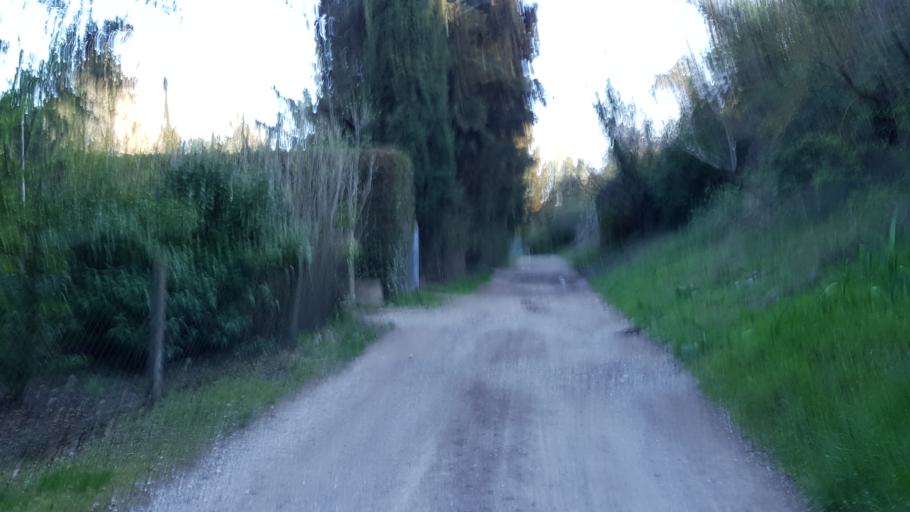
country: FR
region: Provence-Alpes-Cote d'Azur
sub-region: Departement des Bouches-du-Rhone
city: Bouc-Bel-Air
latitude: 43.4845
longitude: 5.4249
